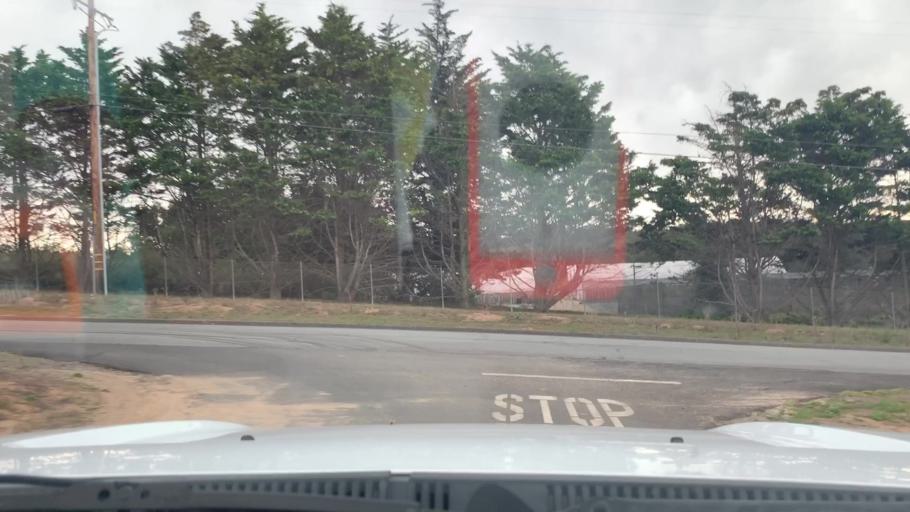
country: US
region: California
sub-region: San Luis Obispo County
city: Callender
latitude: 35.0654
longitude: -120.5610
